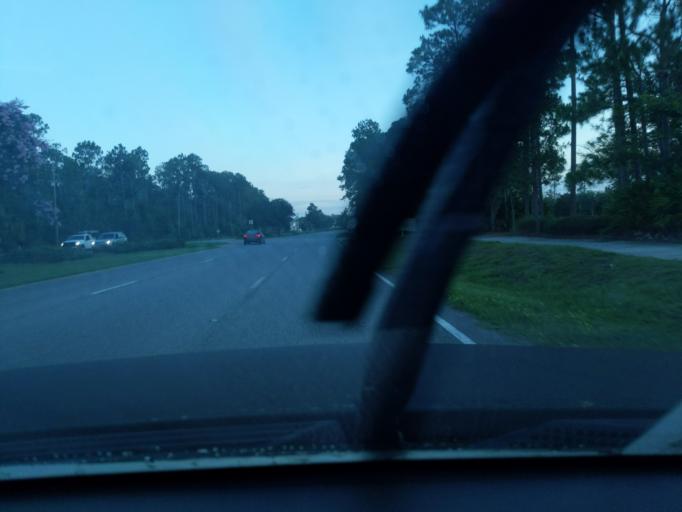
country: US
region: Florida
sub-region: Flagler County
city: Palm Coast
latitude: 29.5466
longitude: -81.2337
